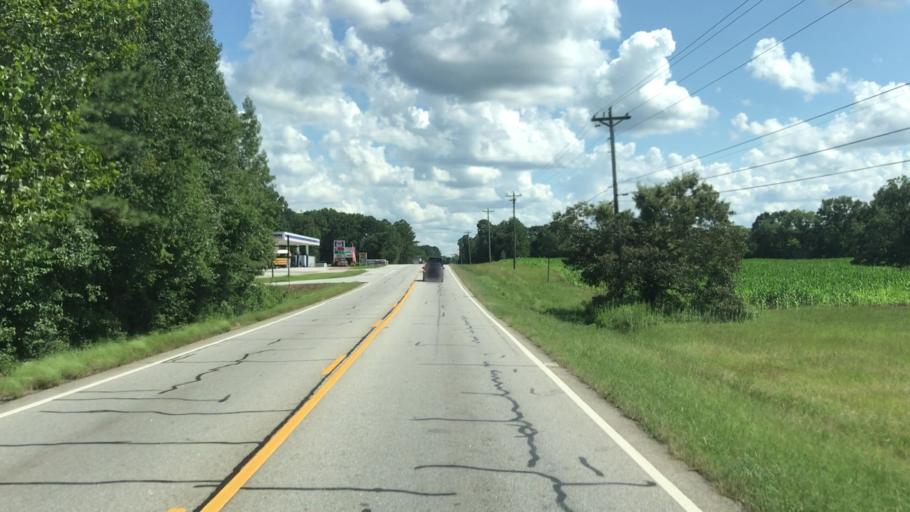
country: US
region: Georgia
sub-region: Walton County
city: Walnut Grove
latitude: 33.7696
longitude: -83.8518
